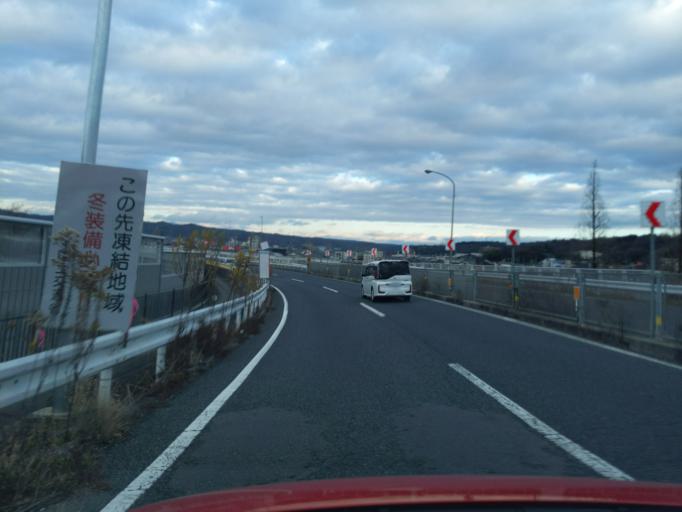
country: JP
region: Gifu
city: Toki
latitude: 35.3493
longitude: 137.1714
